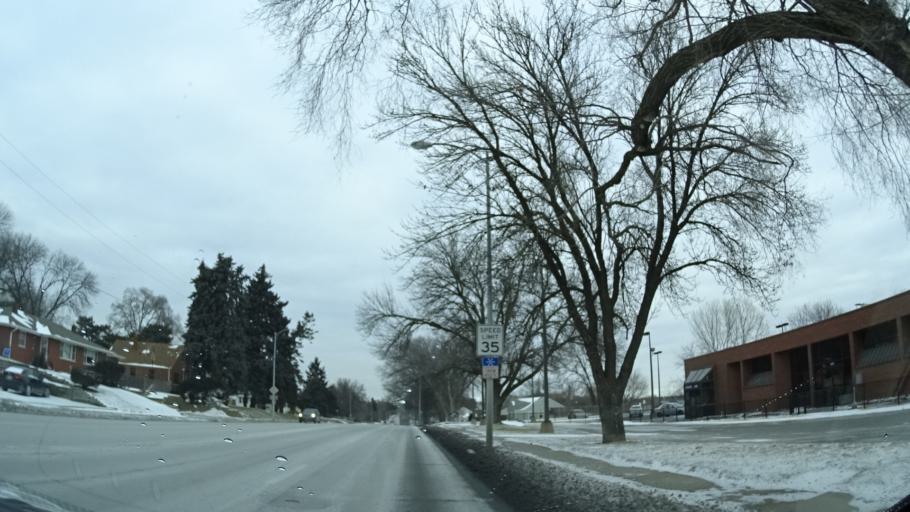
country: US
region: Nebraska
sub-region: Douglas County
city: Omaha
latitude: 41.2285
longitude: -95.9758
